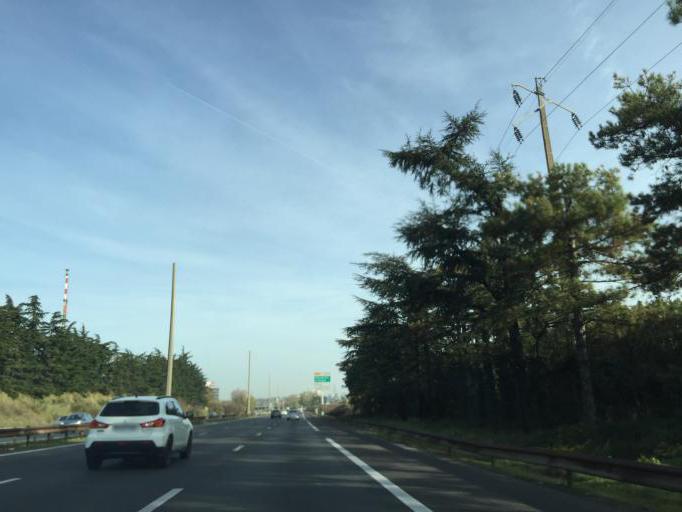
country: FR
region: Rhone-Alpes
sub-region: Departement du Rhone
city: Feyzin
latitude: 45.6667
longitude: 4.8447
